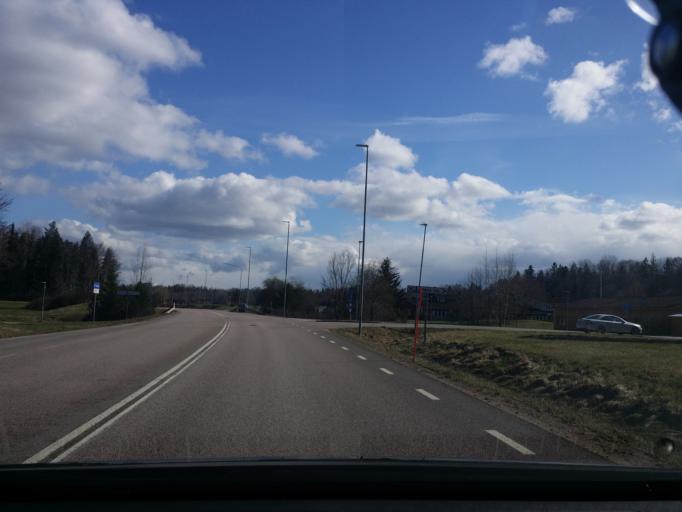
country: SE
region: Vaestmanland
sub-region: Sala Kommun
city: Sala
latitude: 59.9287
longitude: 16.5723
